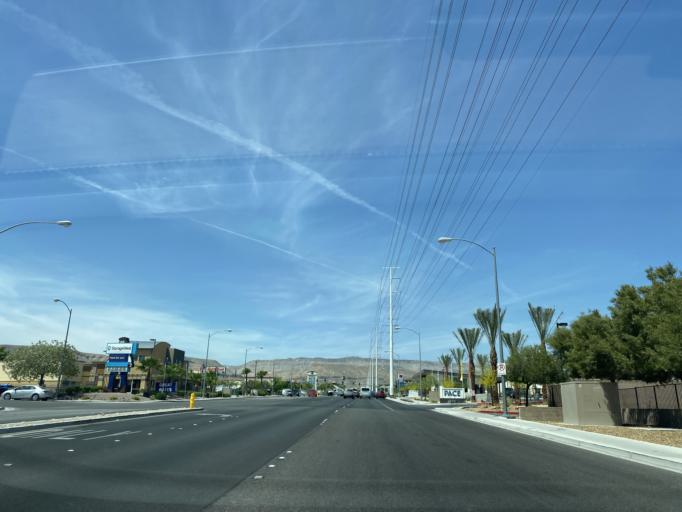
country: US
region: Nevada
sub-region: Clark County
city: Summerlin South
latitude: 36.0852
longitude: -115.2947
